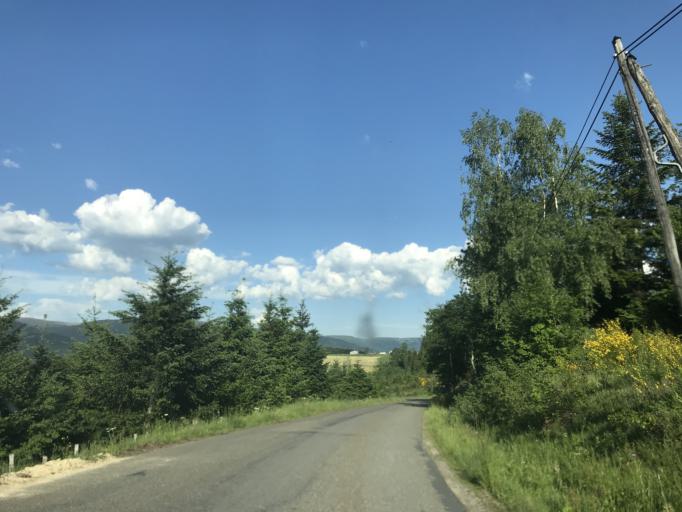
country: FR
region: Auvergne
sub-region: Departement du Puy-de-Dome
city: Job
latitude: 45.6155
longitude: 3.6709
